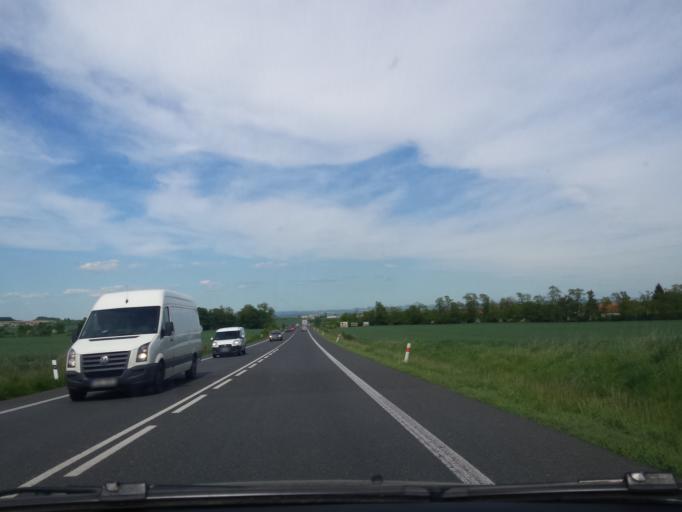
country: CZ
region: Central Bohemia
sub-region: Okres Melnik
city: Veltrusy
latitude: 50.3183
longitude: 14.3322
